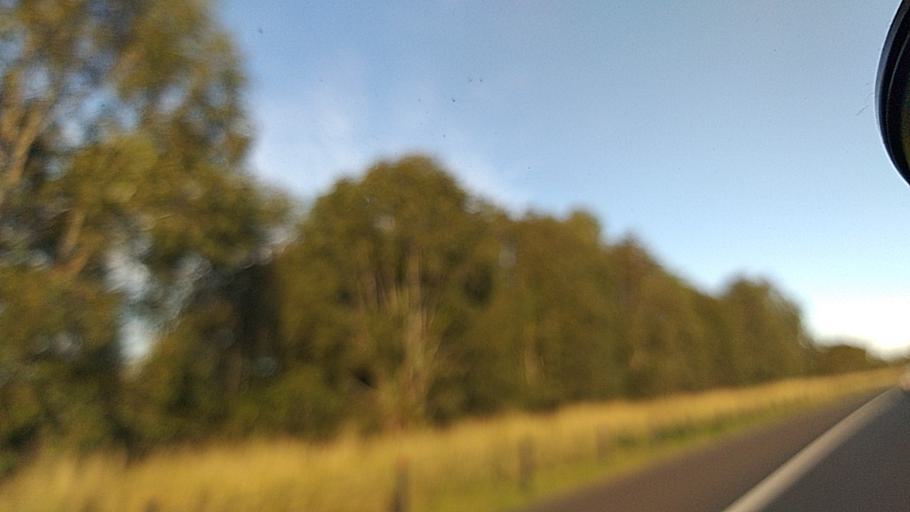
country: AU
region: New South Wales
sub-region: Blacktown
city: Doonside
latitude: -33.7805
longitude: 150.8583
